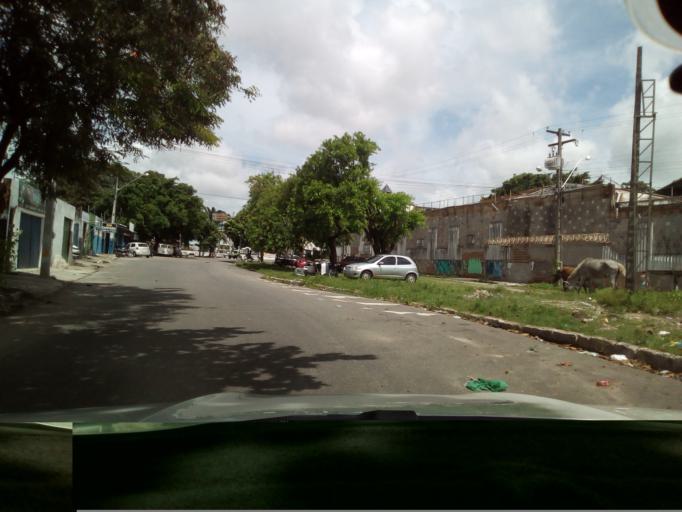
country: BR
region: Paraiba
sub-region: Joao Pessoa
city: Joao Pessoa
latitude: -7.1128
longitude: -34.8869
